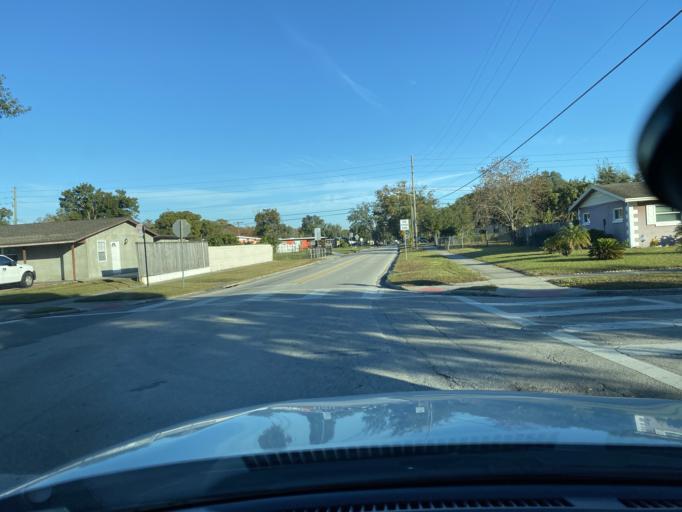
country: US
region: Florida
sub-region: Orange County
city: Azalea Park
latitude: 28.5313
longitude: -81.2990
